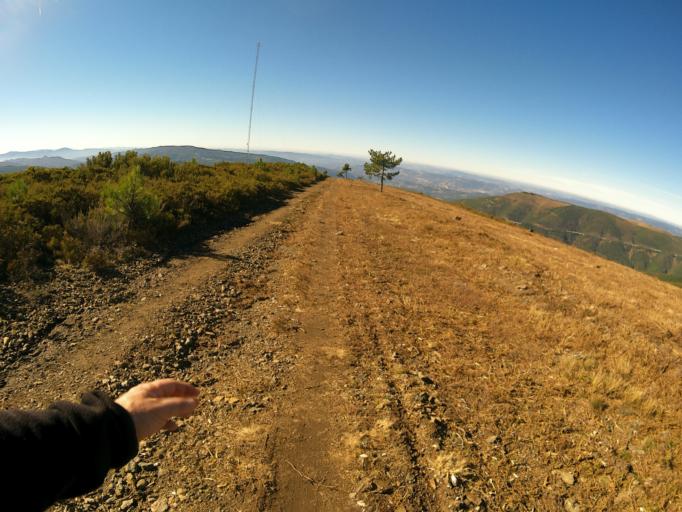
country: PT
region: Vila Real
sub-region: Mesao Frio
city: Mesao Frio
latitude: 41.2500
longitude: -7.9169
